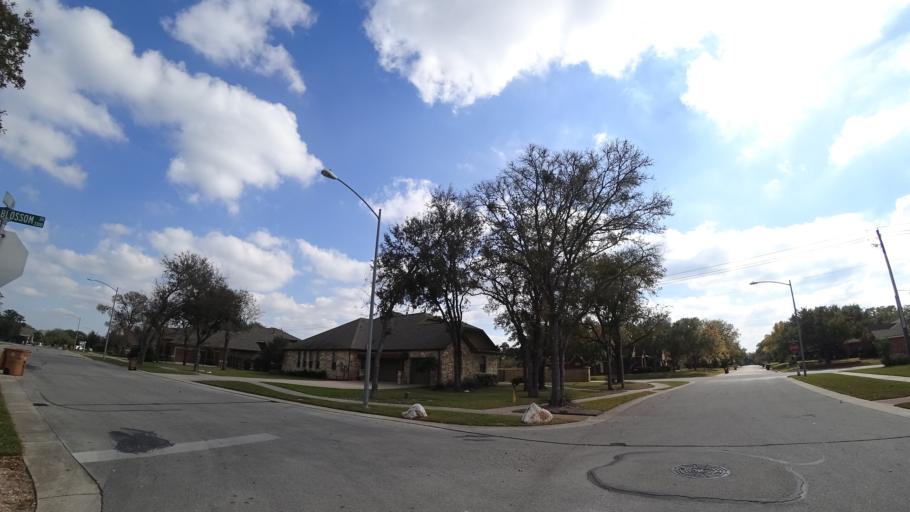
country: US
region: Texas
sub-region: Travis County
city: Shady Hollow
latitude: 30.1737
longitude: -97.8510
